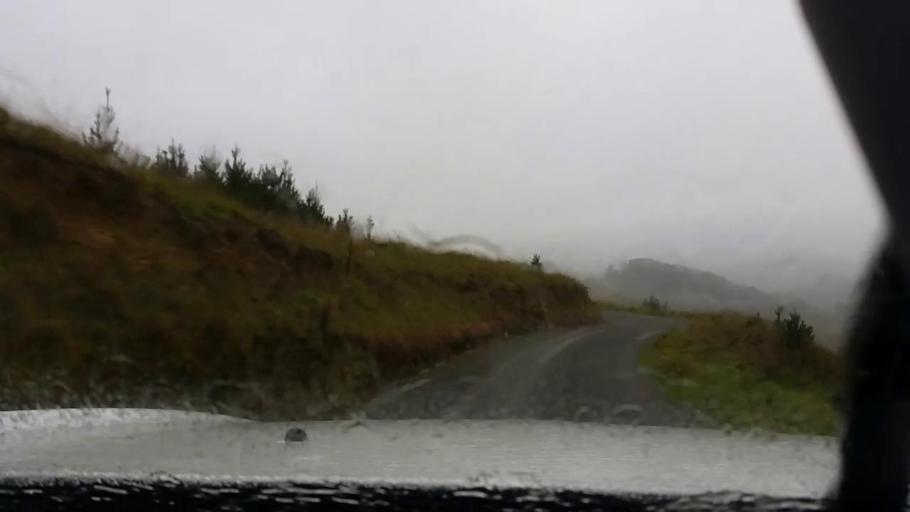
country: NZ
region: Wellington
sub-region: Masterton District
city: Masterton
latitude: -41.1950
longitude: 175.8100
